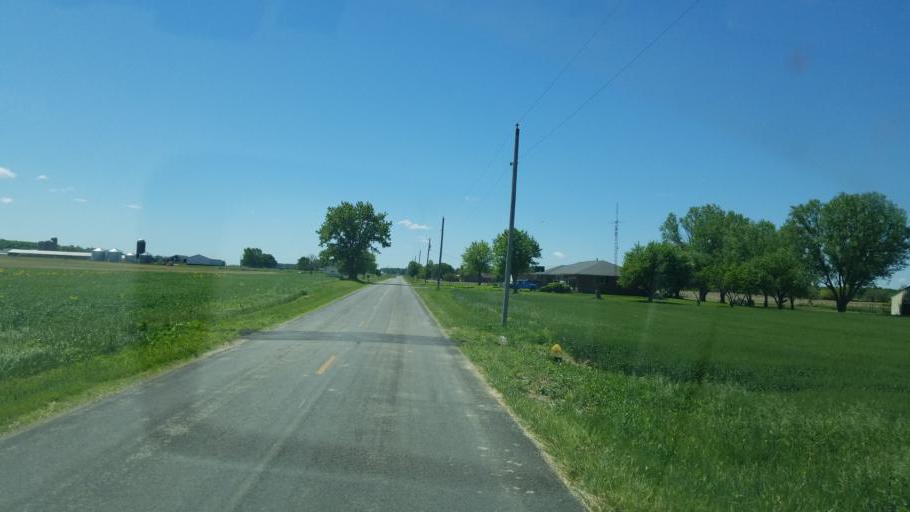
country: US
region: Ohio
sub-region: Shelby County
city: Fort Loramie
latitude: 40.3657
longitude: -84.2975
